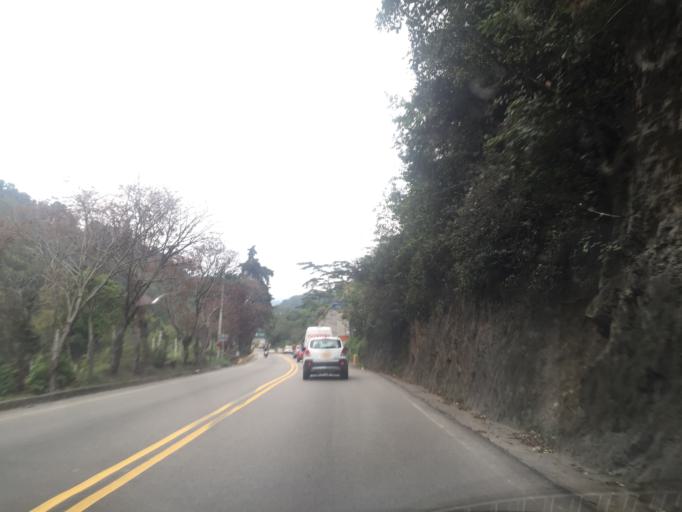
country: CO
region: Tolima
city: Cajamarca
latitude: 4.4348
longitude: -75.4497
